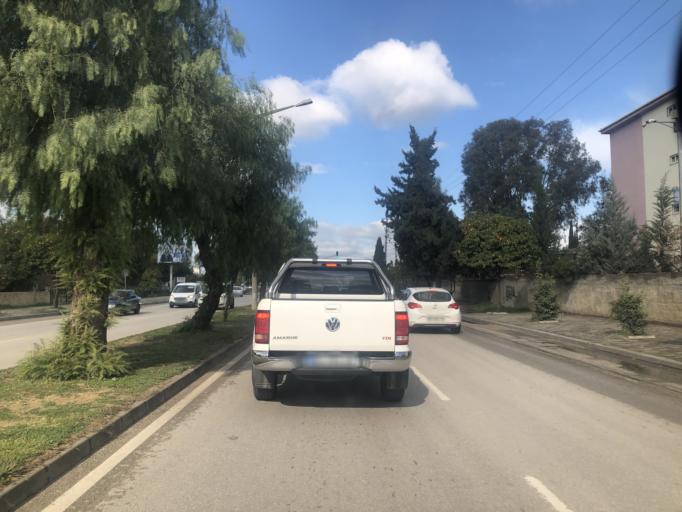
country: TR
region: Adana
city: Adana
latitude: 37.0006
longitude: 35.3417
